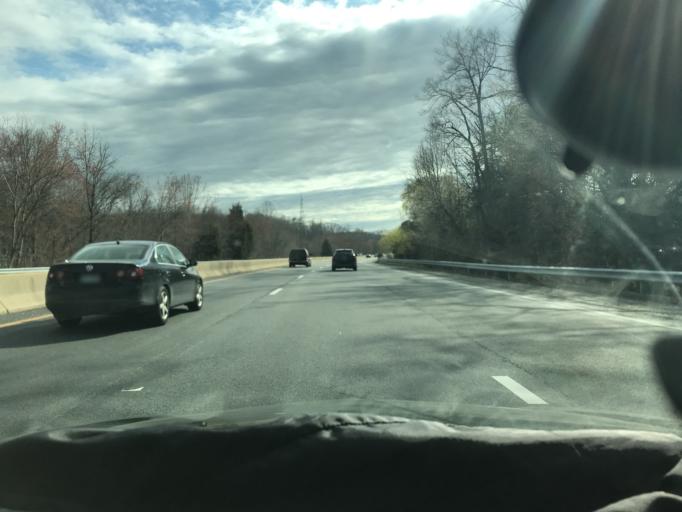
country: US
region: Virginia
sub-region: Chesterfield County
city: Bon Air
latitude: 37.5151
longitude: -77.5361
